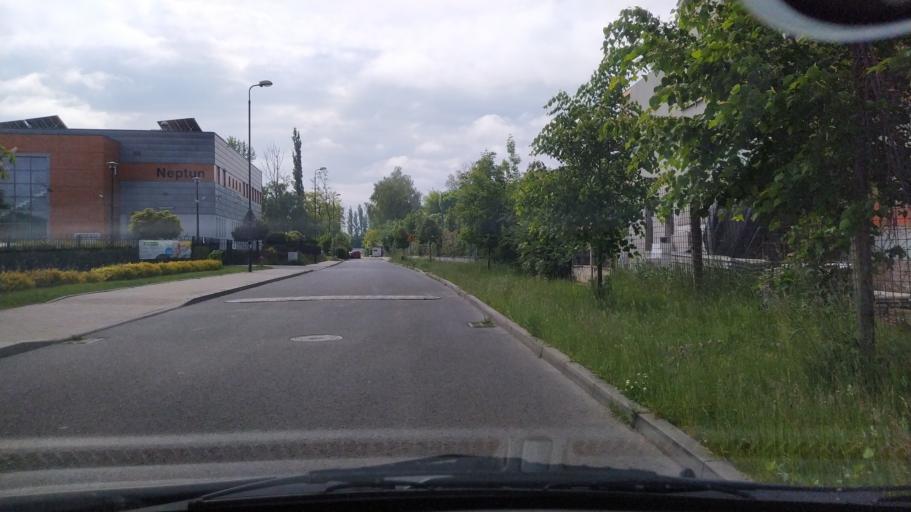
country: PL
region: Silesian Voivodeship
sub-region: Powiat gliwicki
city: Przyszowice
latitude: 50.2869
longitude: 18.7349
